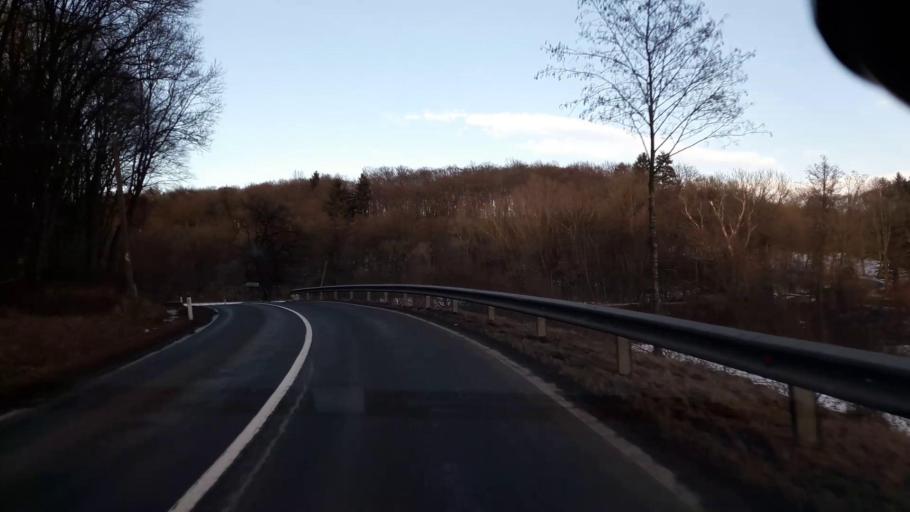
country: AT
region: Lower Austria
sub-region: Politischer Bezirk Wien-Umgebung
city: Mauerbach
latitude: 48.2592
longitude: 16.1692
